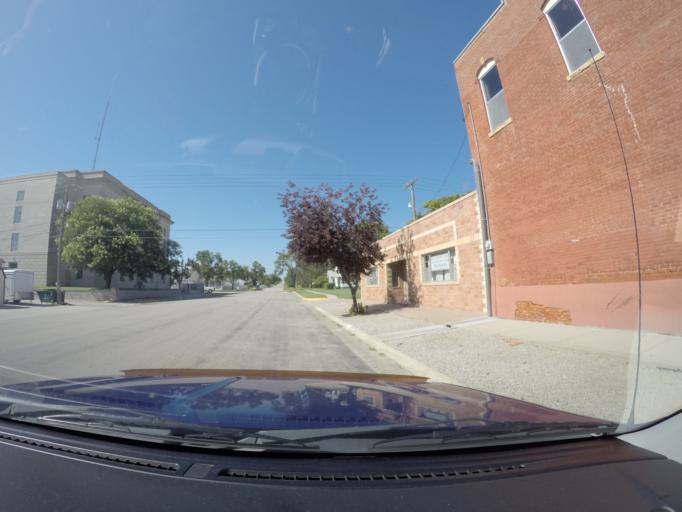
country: US
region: Kansas
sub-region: Rooks County
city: Stockton
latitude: 39.4371
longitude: -99.2737
